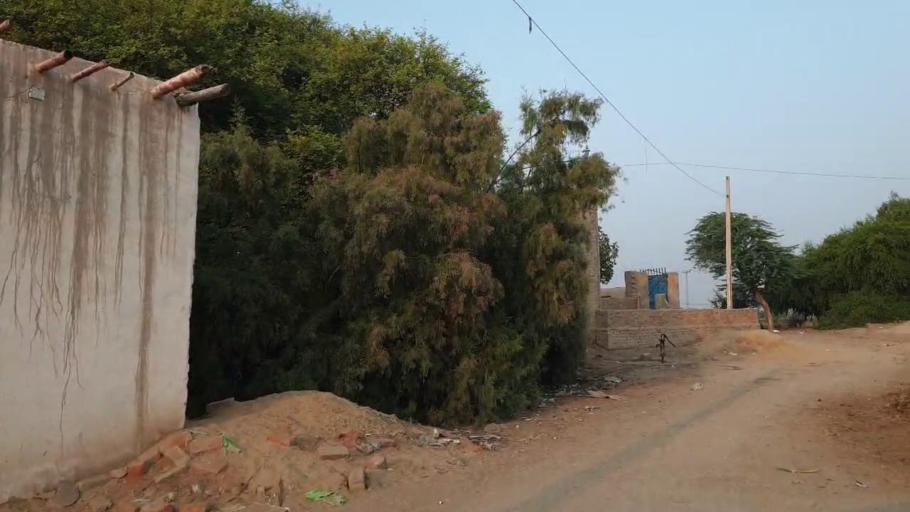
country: PK
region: Sindh
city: Bhan
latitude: 26.4966
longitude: 67.7281
